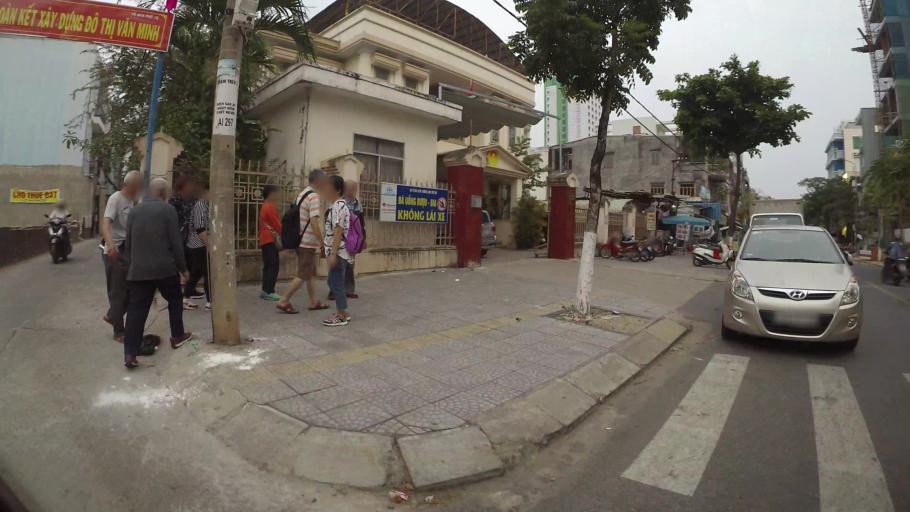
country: VN
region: Da Nang
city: Da Nang
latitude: 16.0628
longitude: 108.2221
